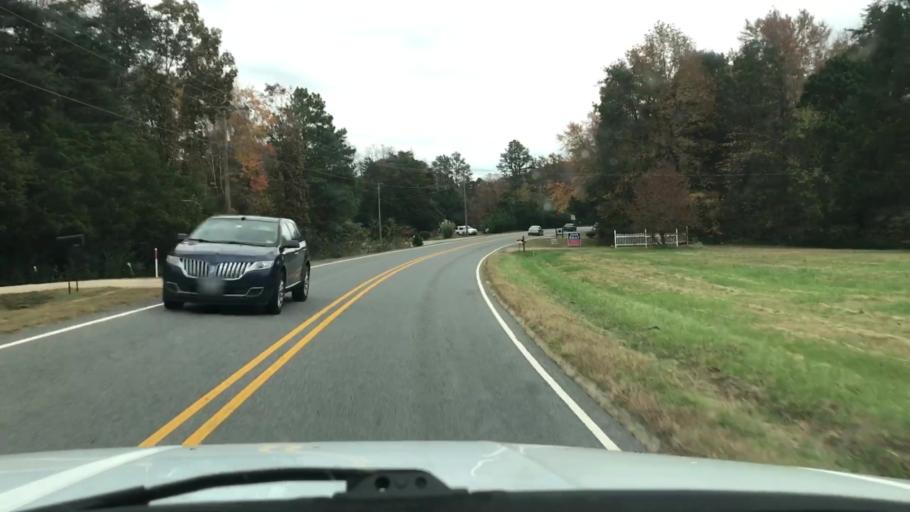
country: US
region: Virginia
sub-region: Goochland County
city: Goochland
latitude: 37.6357
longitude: -77.7916
